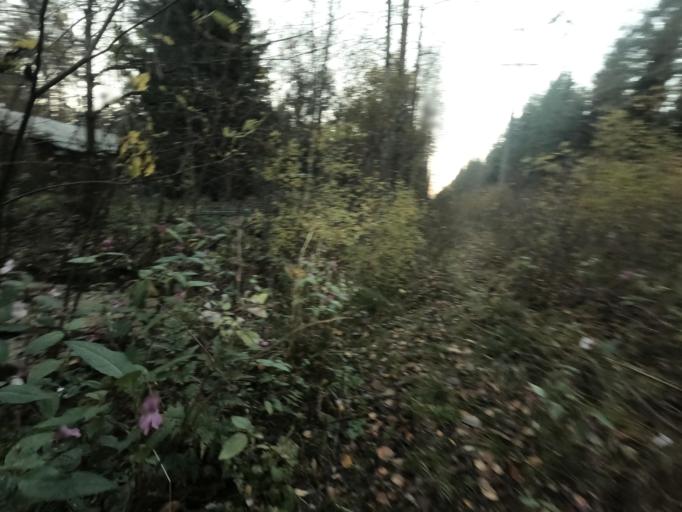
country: RU
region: St.-Petersburg
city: Komarovo
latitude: 60.2009
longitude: 29.8135
